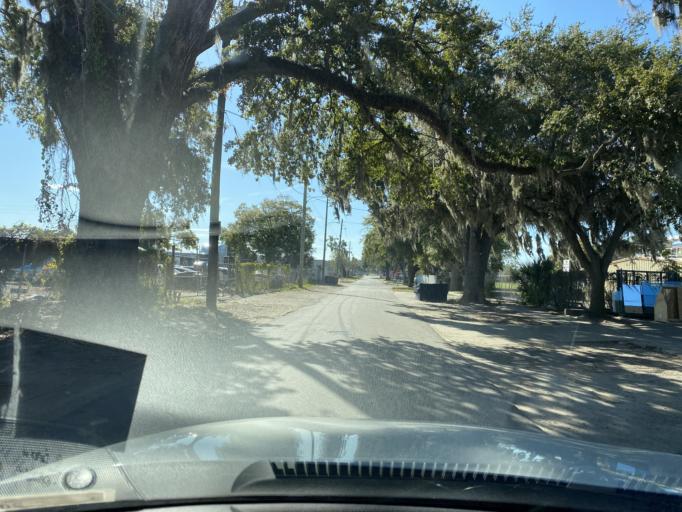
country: US
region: Florida
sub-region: Orange County
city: Orlando
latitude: 28.5429
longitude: -81.3994
